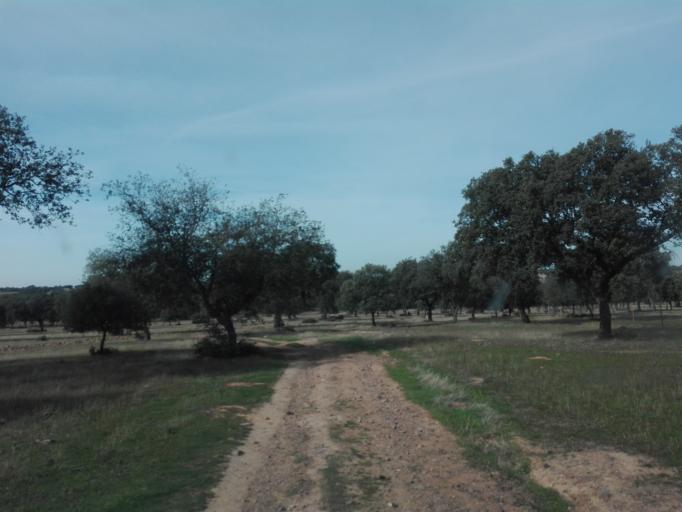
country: ES
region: Extremadura
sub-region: Provincia de Badajoz
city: Campillo de Llerena
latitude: 38.4672
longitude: -5.8871
